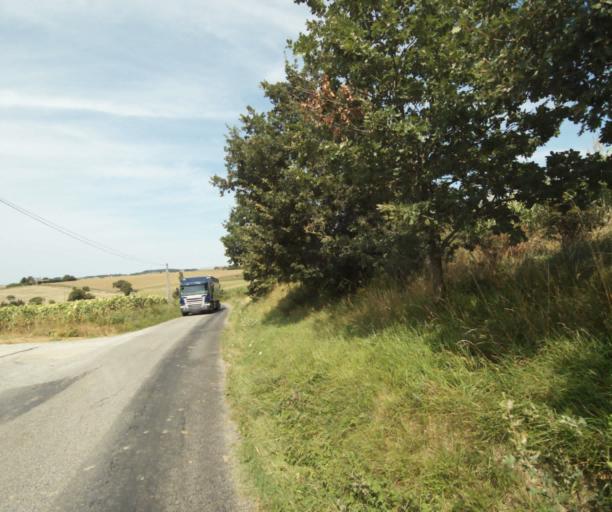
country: FR
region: Midi-Pyrenees
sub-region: Departement de la Haute-Garonne
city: Gaillac-Toulza
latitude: 43.2520
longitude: 1.4193
